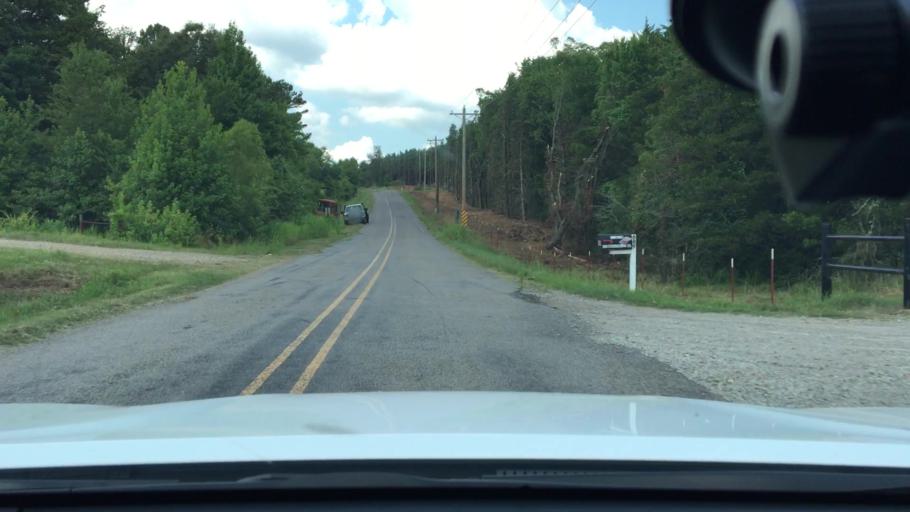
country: US
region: Arkansas
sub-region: Logan County
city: Paris
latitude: 35.2693
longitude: -93.6713
